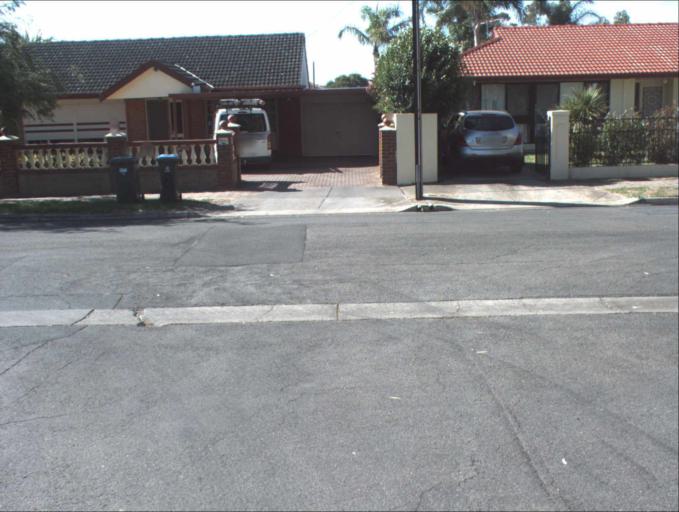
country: AU
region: South Australia
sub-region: Port Adelaide Enfield
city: Klemzig
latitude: -34.8685
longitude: 138.6379
